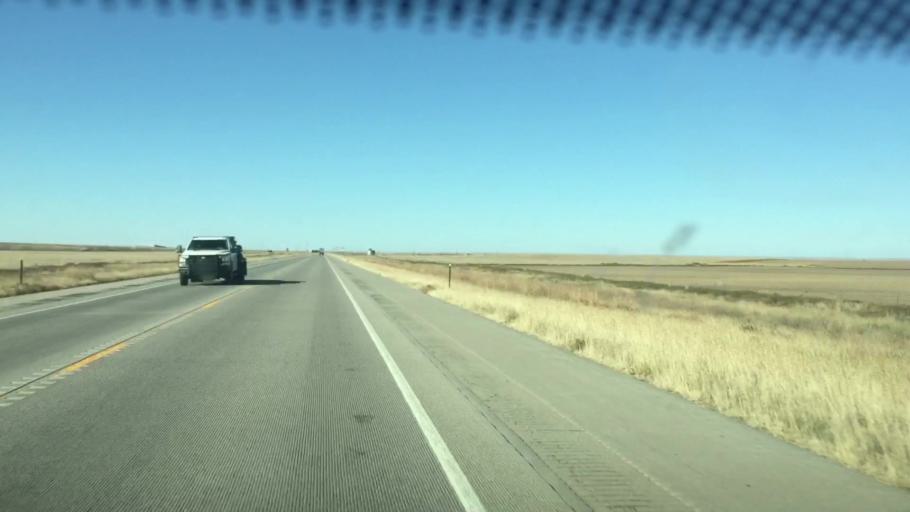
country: US
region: Colorado
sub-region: Kiowa County
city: Eads
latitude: 38.7521
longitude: -102.7768
